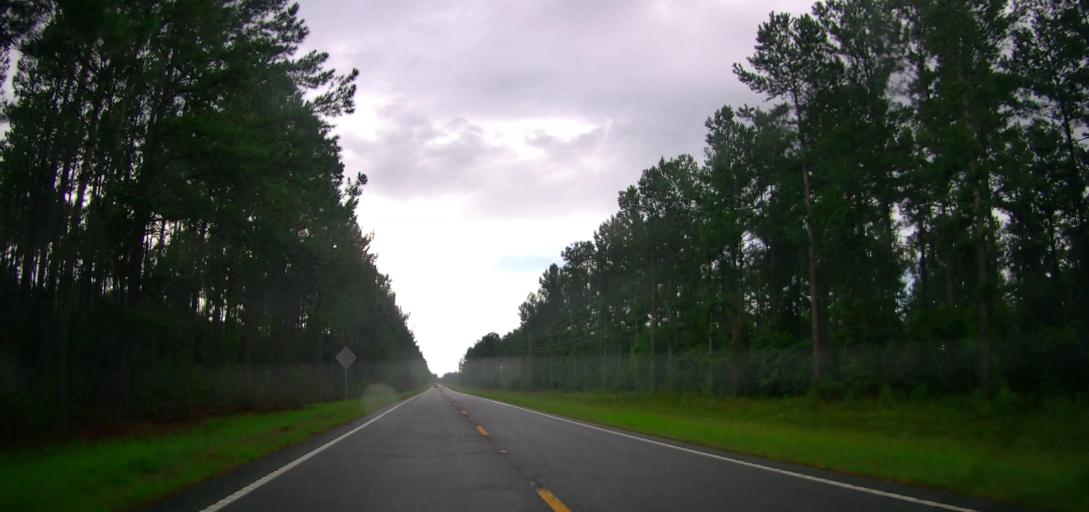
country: US
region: Georgia
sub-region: Ware County
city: Deenwood
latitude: 31.2751
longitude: -82.5319
